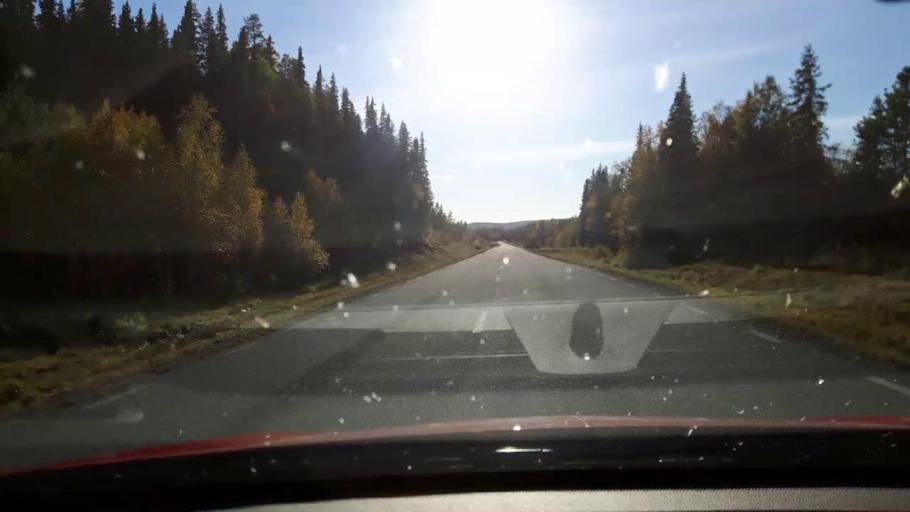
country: SE
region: Jaemtland
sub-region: OEstersunds Kommun
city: Lit
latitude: 63.8594
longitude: 14.9555
